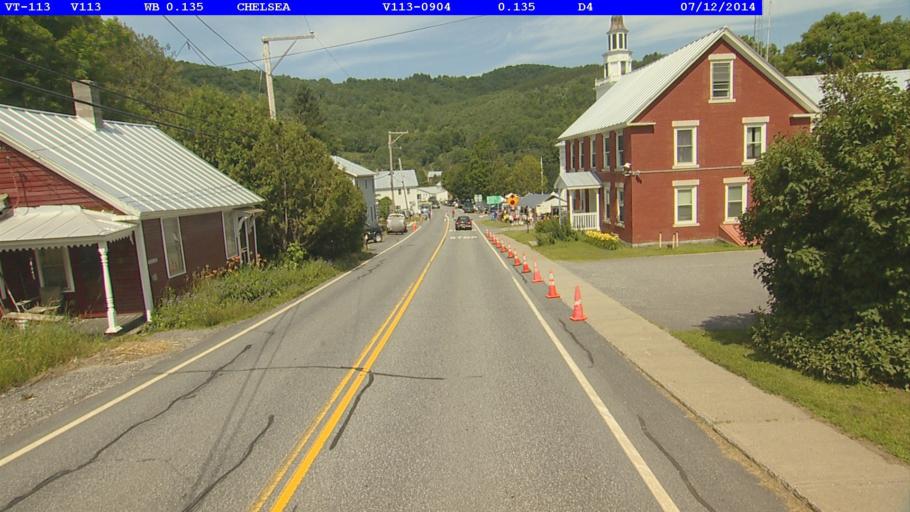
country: US
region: Vermont
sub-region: Orange County
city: Chelsea
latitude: 43.9879
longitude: -72.4454
